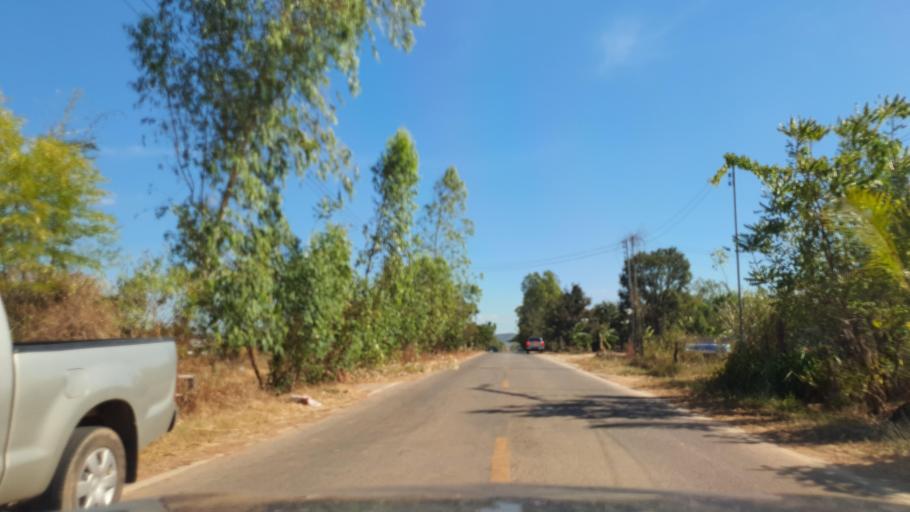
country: TH
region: Kalasin
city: Khao Wong
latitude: 16.7254
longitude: 104.1017
